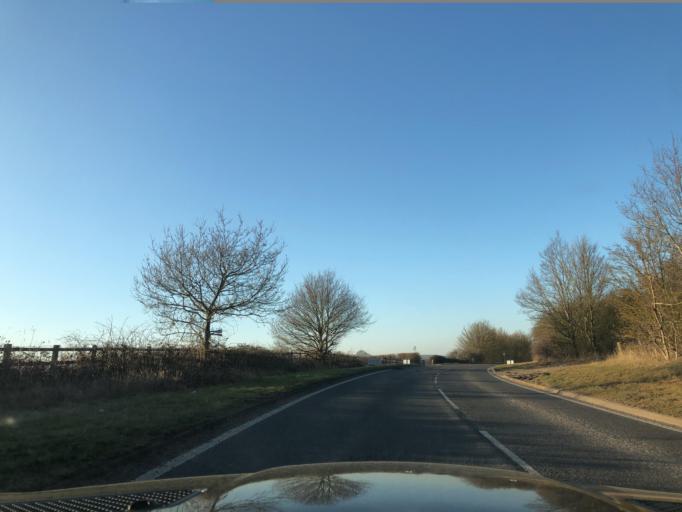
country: GB
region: England
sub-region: Warwickshire
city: Warwick
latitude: 52.2633
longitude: -1.6294
